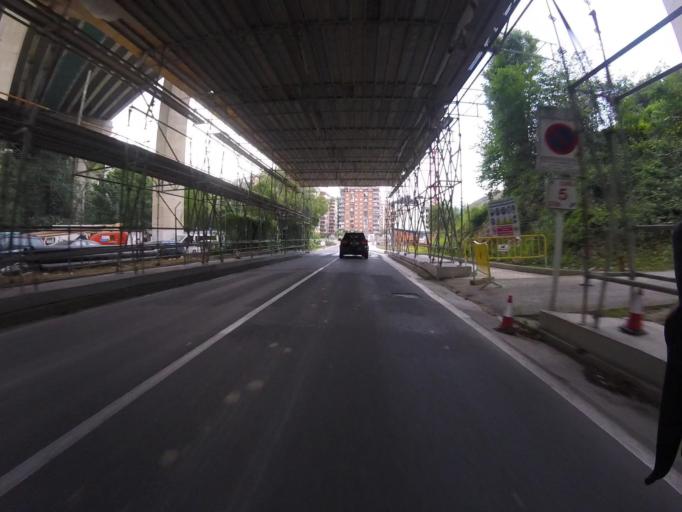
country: ES
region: Basque Country
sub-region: Provincia de Guipuzcoa
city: Errenteria
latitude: 43.3076
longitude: -1.9045
